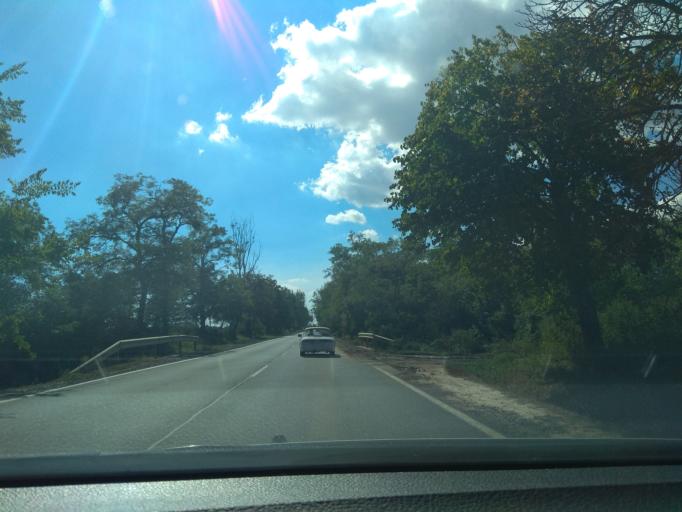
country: HU
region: Borsod-Abauj-Zemplen
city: Tolcsva
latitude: 48.2948
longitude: 21.5131
